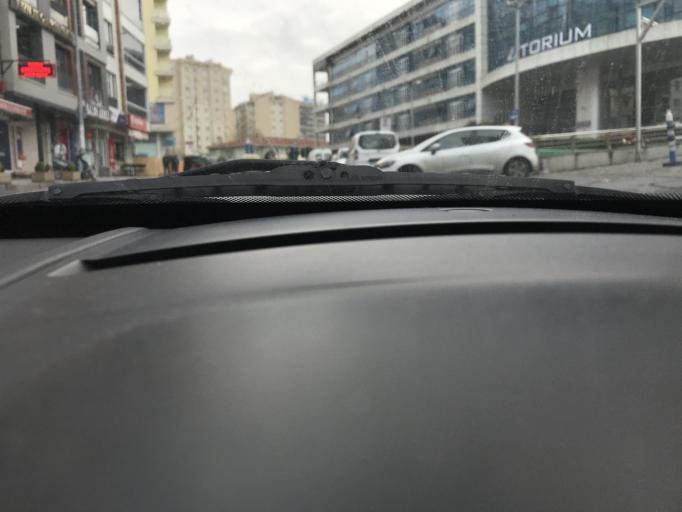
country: TR
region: Istanbul
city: Yakuplu
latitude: 41.0053
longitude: 28.6901
